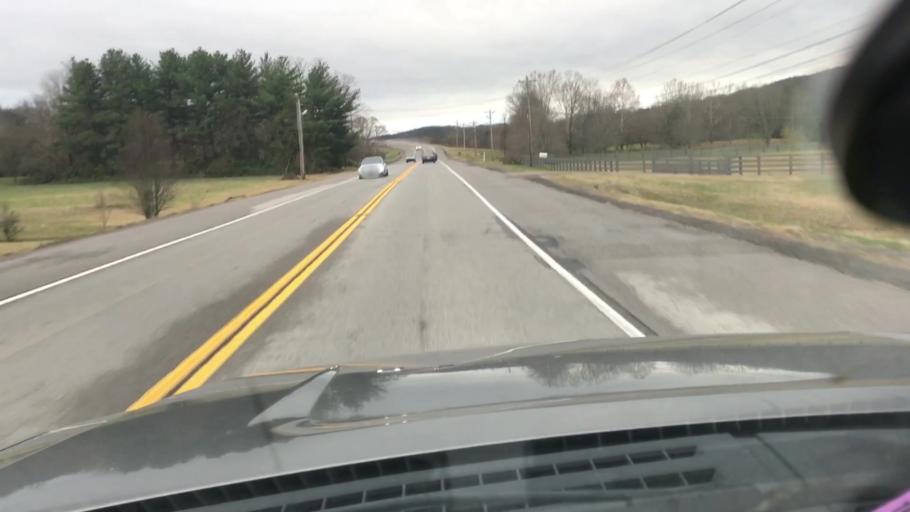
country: US
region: Tennessee
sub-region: Williamson County
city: Brentwood Estates
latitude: 35.9645
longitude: -86.7719
